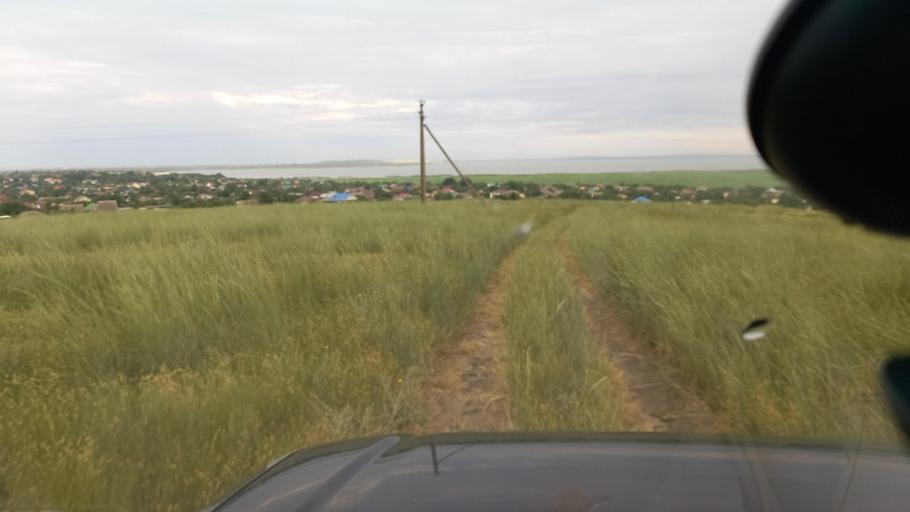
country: RU
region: Krasnodarskiy
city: Akhtanizovskaya
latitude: 45.3126
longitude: 37.0837
